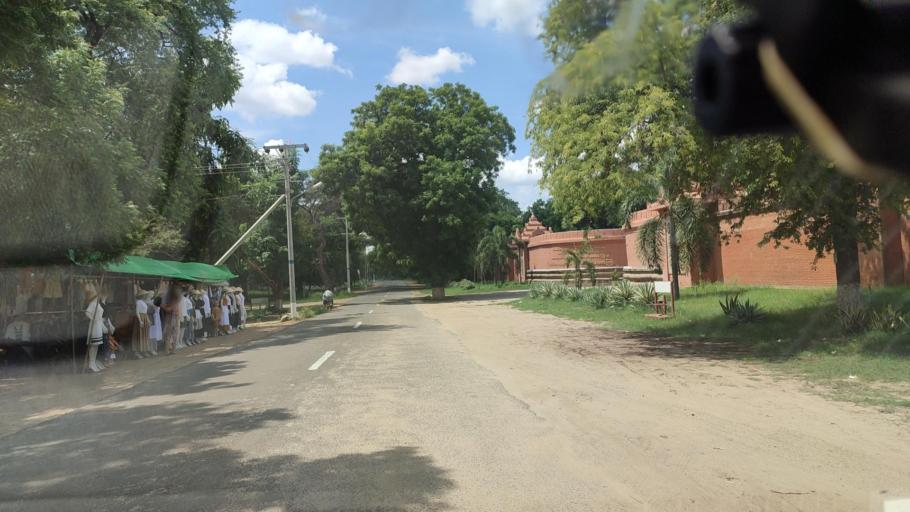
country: MM
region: Magway
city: Pakokku
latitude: 21.1721
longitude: 94.8637
